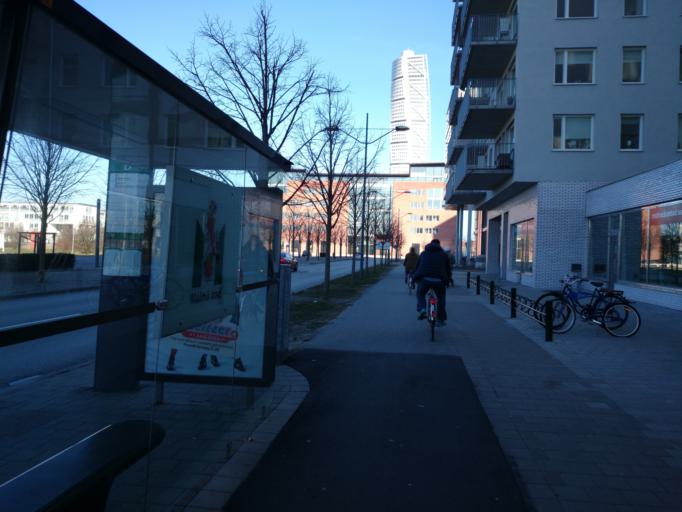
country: SE
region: Skane
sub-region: Malmo
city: Malmoe
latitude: 55.6082
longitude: 12.9787
